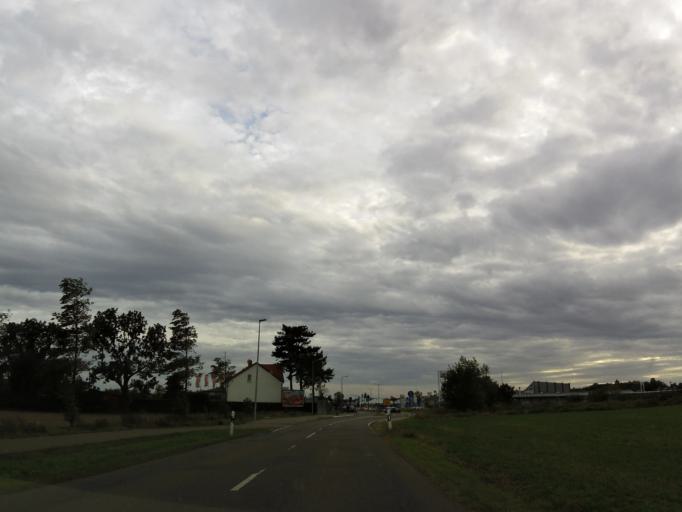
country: DE
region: Saxony
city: Schkeuditz
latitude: 51.3491
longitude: 12.2631
